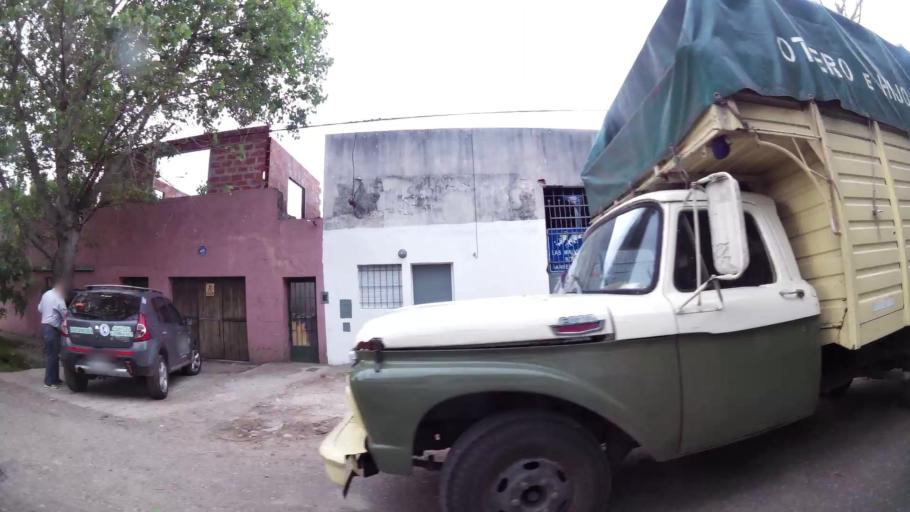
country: AR
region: Santa Fe
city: Gobernador Galvez
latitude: -32.9988
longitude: -60.6774
